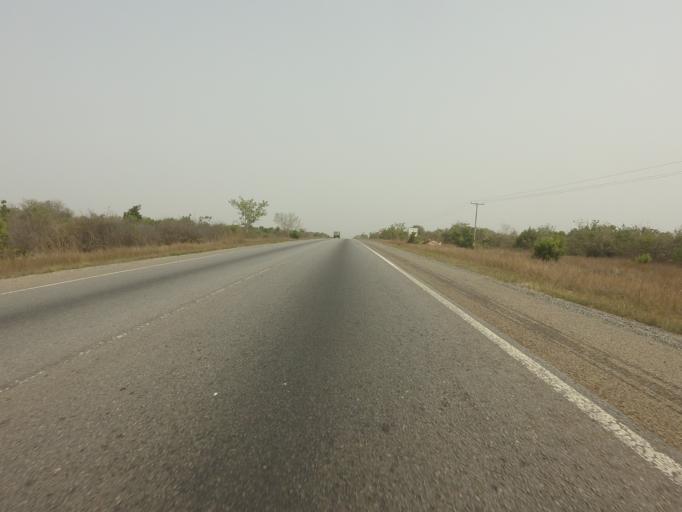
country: GH
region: Greater Accra
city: Tema
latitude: 5.8695
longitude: 0.3176
